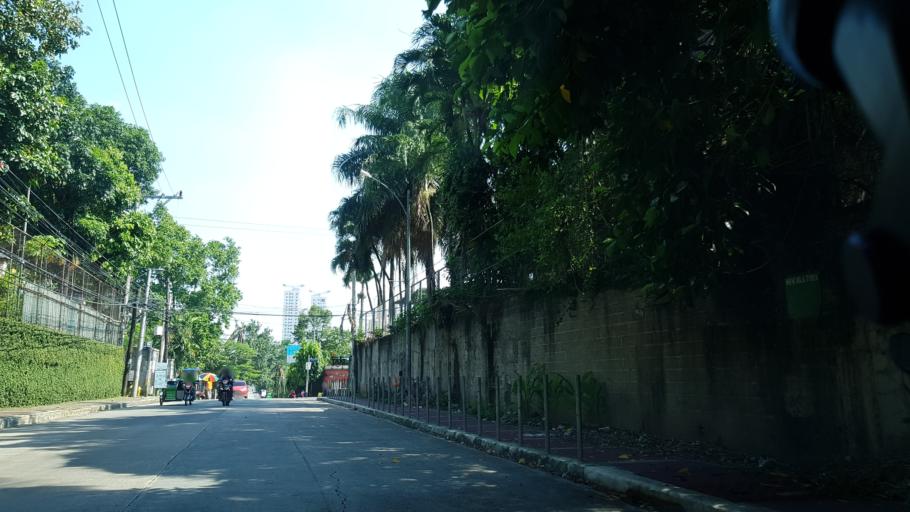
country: PH
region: Metro Manila
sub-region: San Juan
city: San Juan
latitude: 14.6172
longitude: 121.0268
